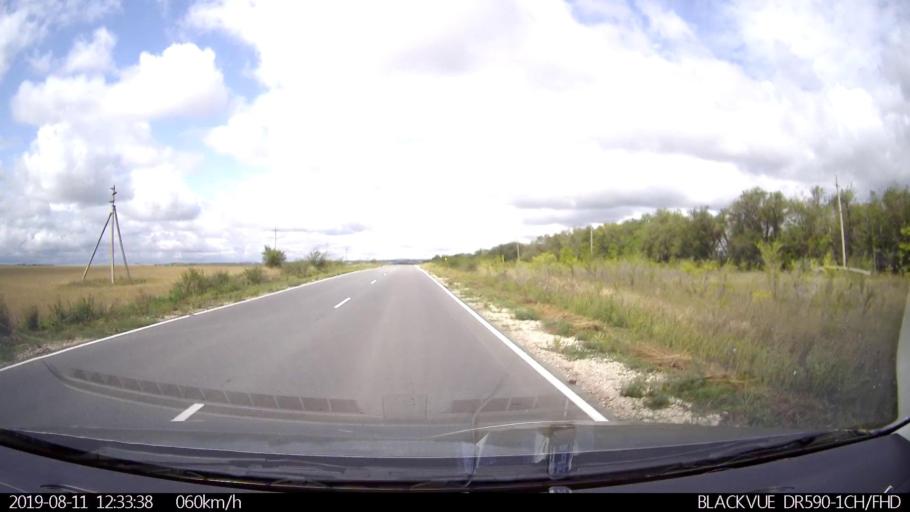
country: RU
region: Ulyanovsk
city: Ignatovka
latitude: 53.8109
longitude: 47.8534
